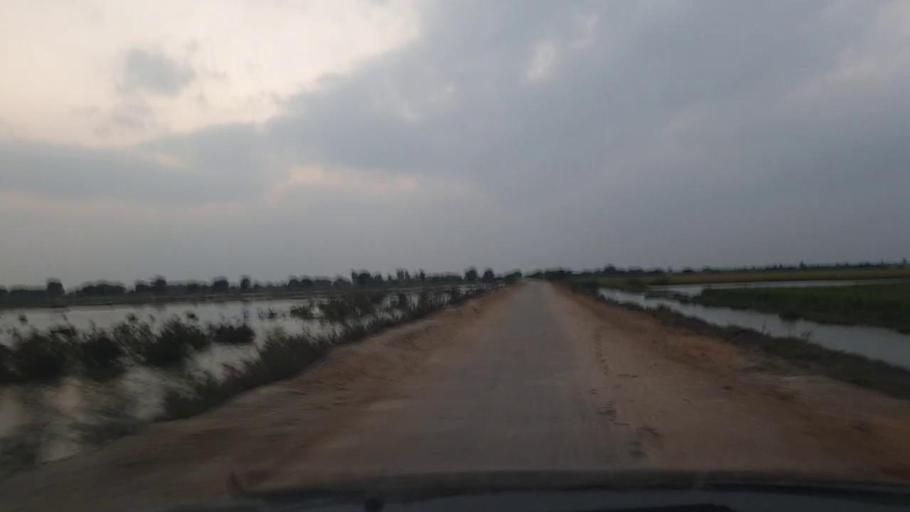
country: PK
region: Sindh
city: Jati
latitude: 24.5210
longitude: 68.3744
